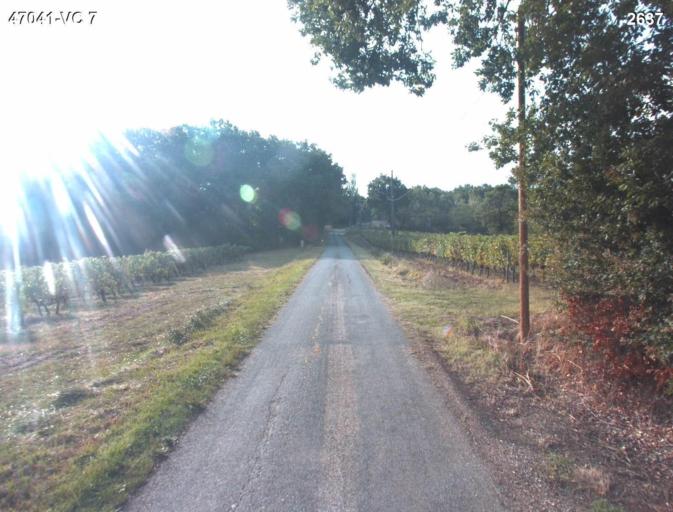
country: FR
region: Aquitaine
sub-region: Departement du Lot-et-Garonne
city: Port-Sainte-Marie
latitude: 44.1878
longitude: 0.4241
